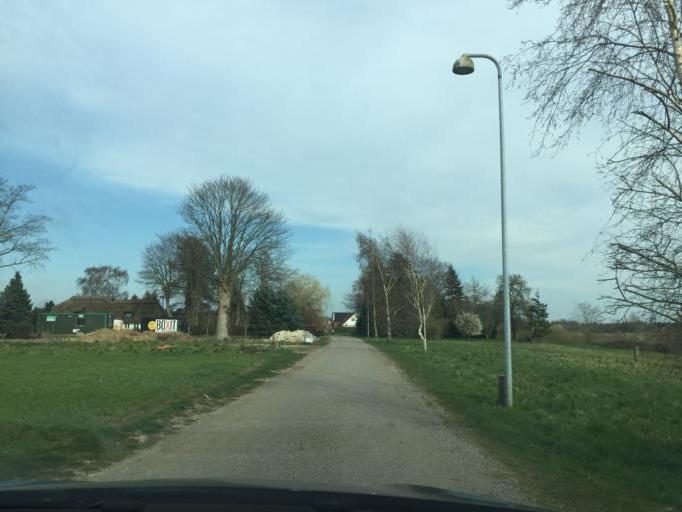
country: DK
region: South Denmark
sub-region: Faaborg-Midtfyn Kommune
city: Arslev
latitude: 55.3222
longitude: 10.5148
